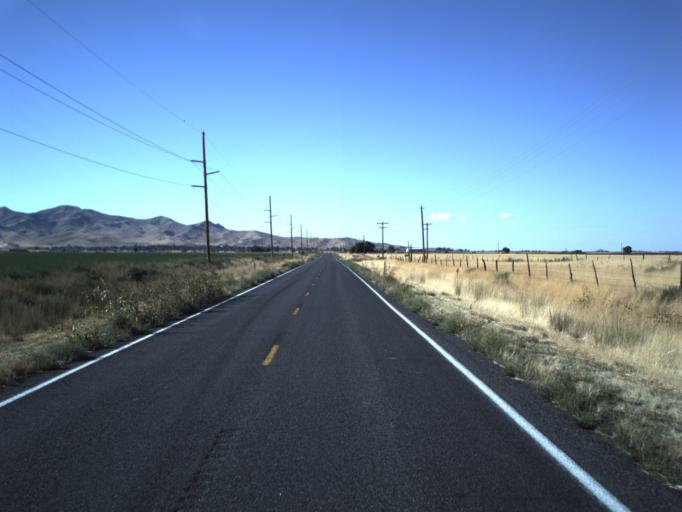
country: US
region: Utah
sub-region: Millard County
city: Delta
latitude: 39.4152
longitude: -112.3300
